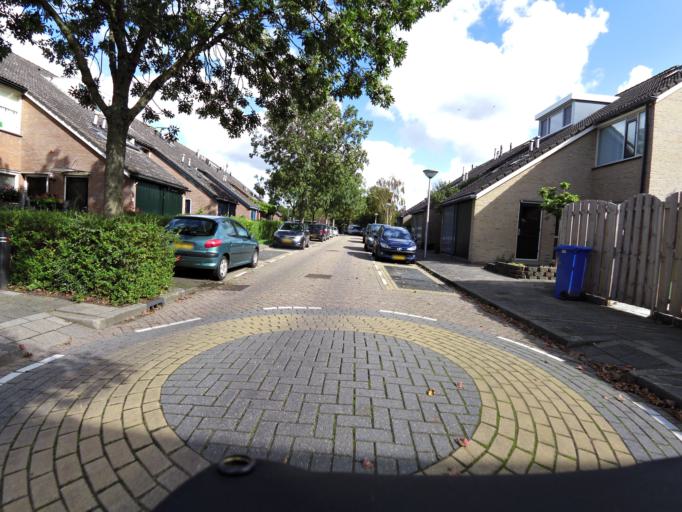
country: NL
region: South Holland
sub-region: Gemeente Delft
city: Delft
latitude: 51.9776
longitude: 4.3141
